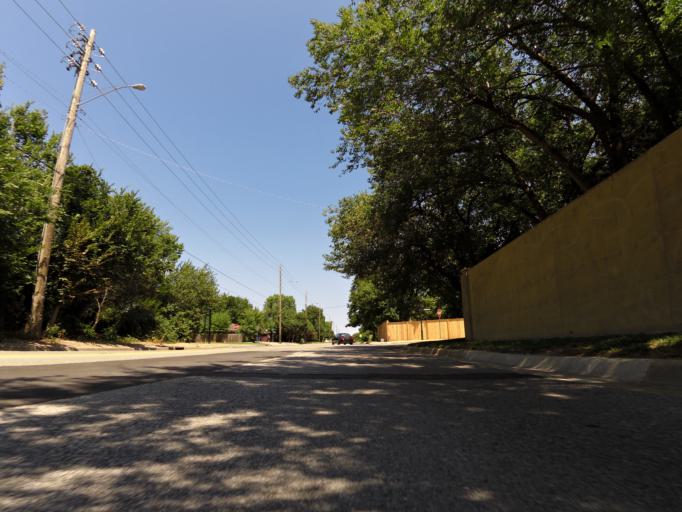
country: US
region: Kansas
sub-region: Sedgwick County
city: Bellaire
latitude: 37.6895
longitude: -97.2622
